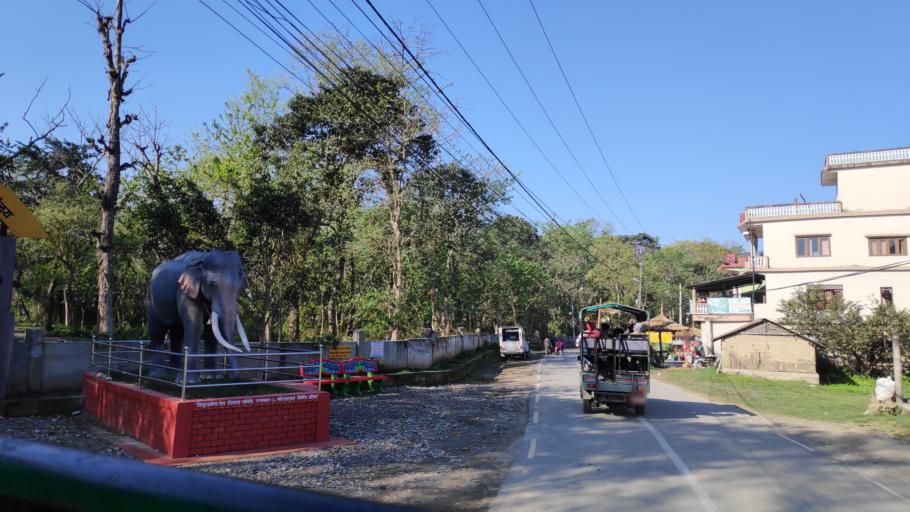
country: NP
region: Central Region
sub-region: Narayani Zone
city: Bharatpur
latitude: 27.5744
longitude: 84.5004
